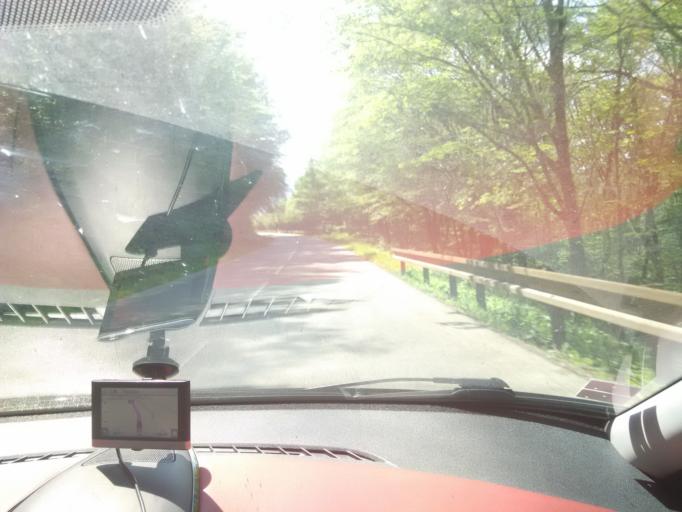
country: SK
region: Banskobystricky
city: Revuca
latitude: 48.6292
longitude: 20.2602
